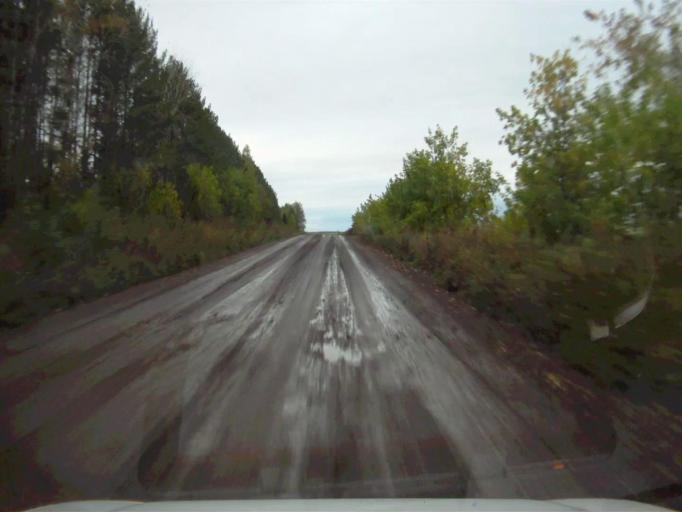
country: RU
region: Sverdlovsk
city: Mikhaylovsk
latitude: 56.1556
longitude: 59.2597
